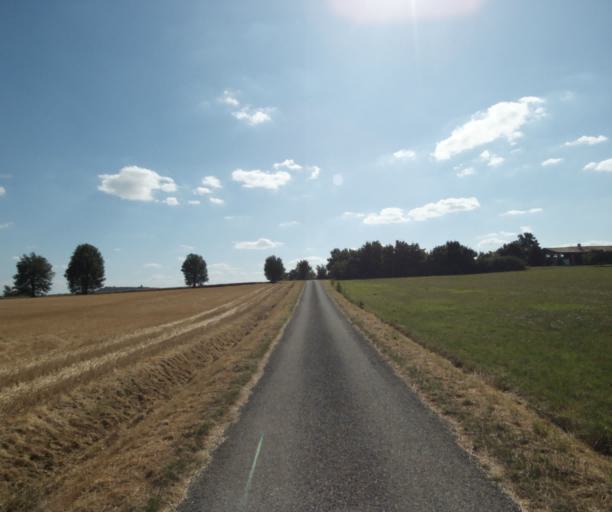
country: FR
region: Midi-Pyrenees
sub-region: Departement de la Haute-Garonne
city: Saint-Felix-Lauragais
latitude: 43.4781
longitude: 1.9068
